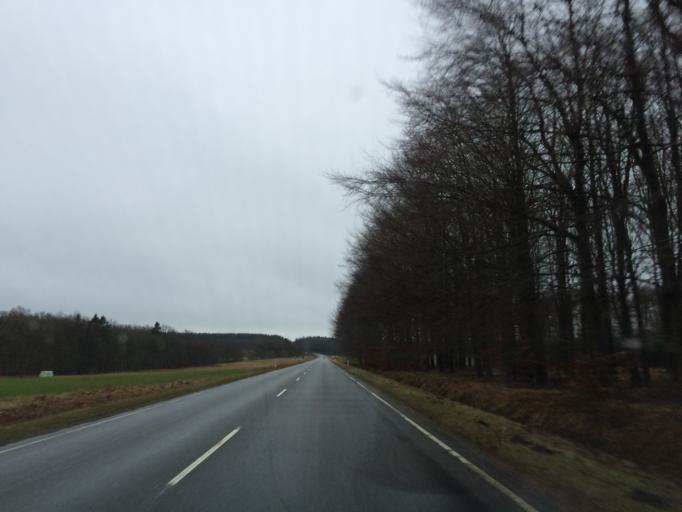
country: DK
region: North Denmark
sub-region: Mariagerfjord Kommune
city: Arden
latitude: 56.8116
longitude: 9.8188
